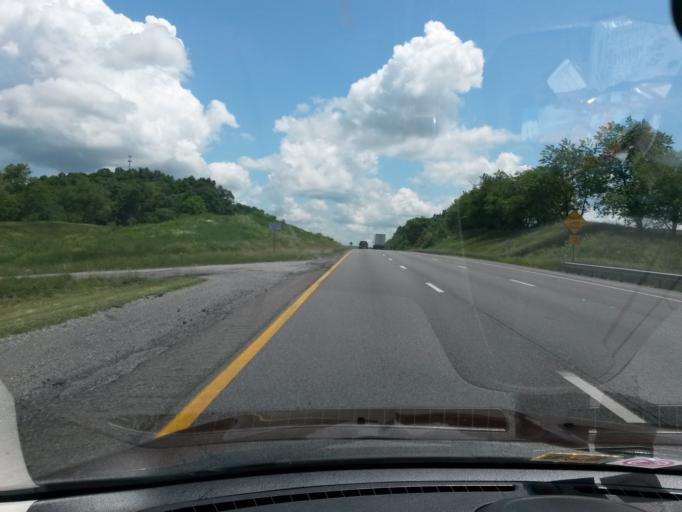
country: US
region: Virginia
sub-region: Wythe County
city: Wytheville
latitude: 36.9431
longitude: -80.9185
